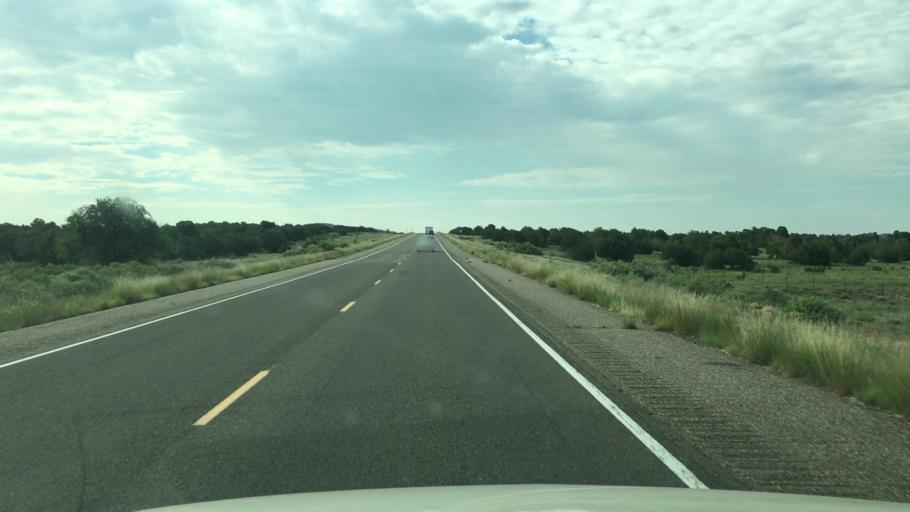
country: US
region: New Mexico
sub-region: Santa Fe County
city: Eldorado at Santa Fe
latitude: 35.3375
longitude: -105.8385
